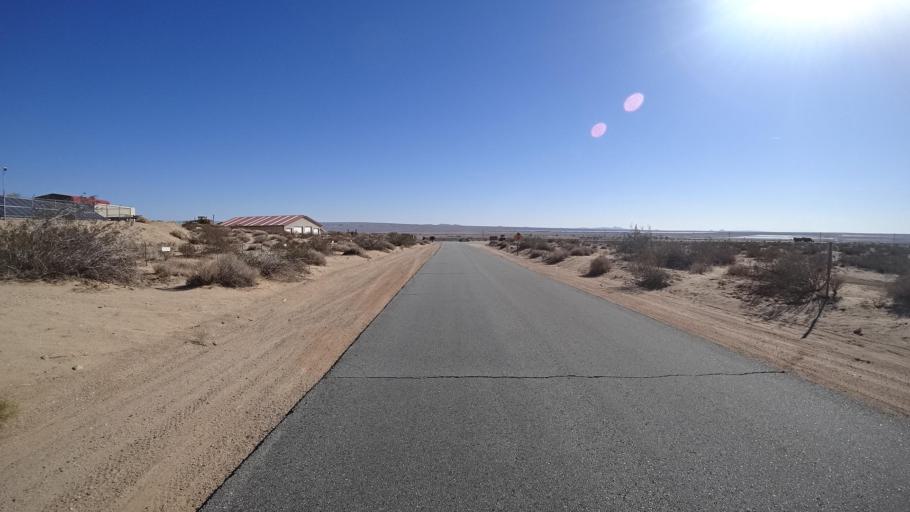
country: US
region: California
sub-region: Kern County
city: California City
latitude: 35.3016
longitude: -118.0035
